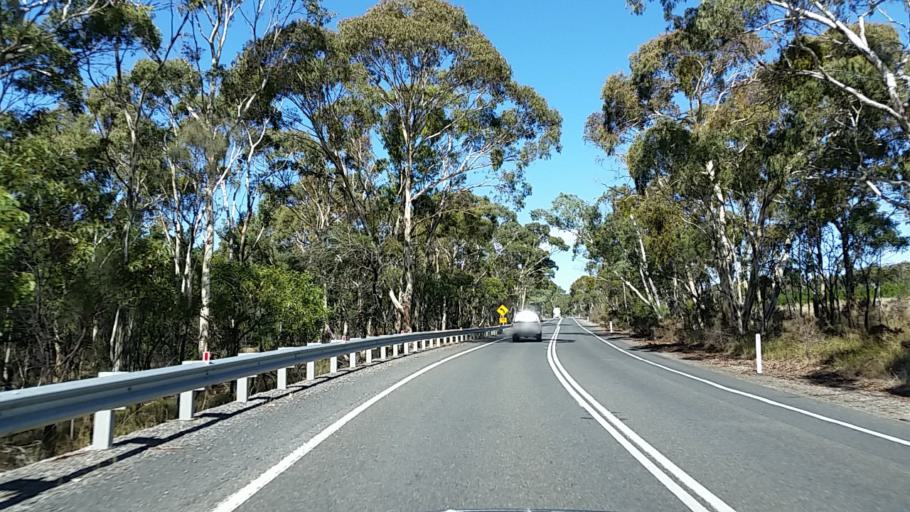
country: AU
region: South Australia
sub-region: Adelaide Hills
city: Birdwood
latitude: -34.7410
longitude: 138.9799
